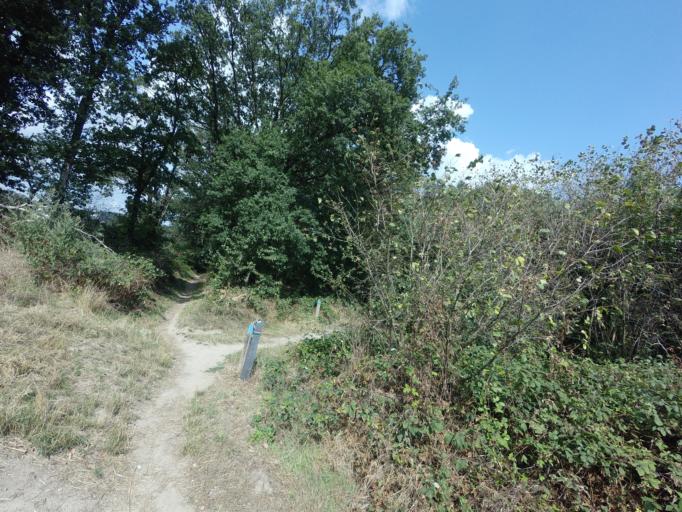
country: NL
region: Limburg
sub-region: Gemeente Heerlen
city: Heerlen
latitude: 50.9086
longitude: 6.0008
